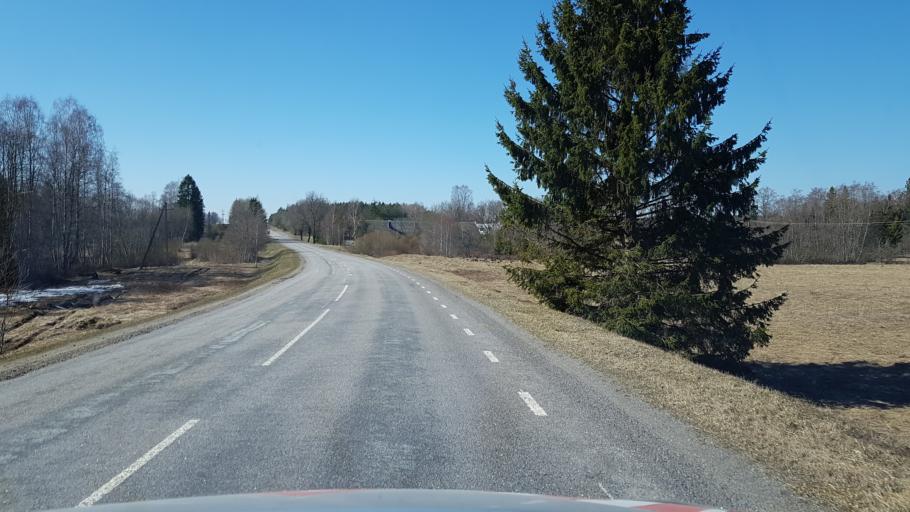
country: EE
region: Laeaene-Virumaa
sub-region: Vaeike-Maarja vald
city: Vaike-Maarja
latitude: 59.1563
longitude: 26.2128
